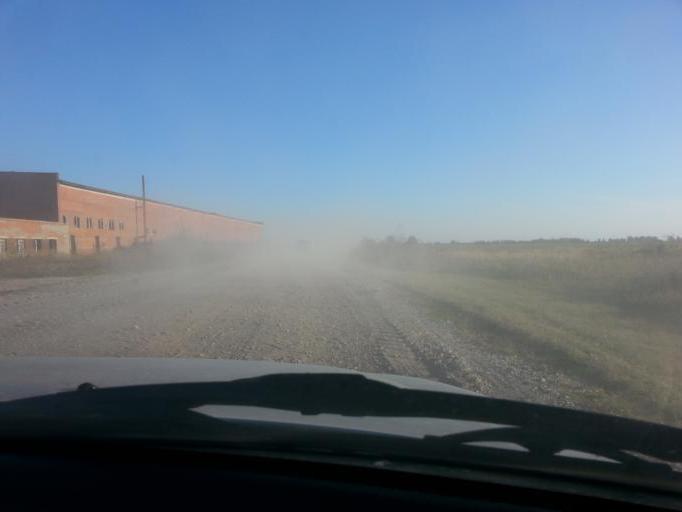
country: LV
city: Tervete
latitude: 56.6135
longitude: 23.4761
